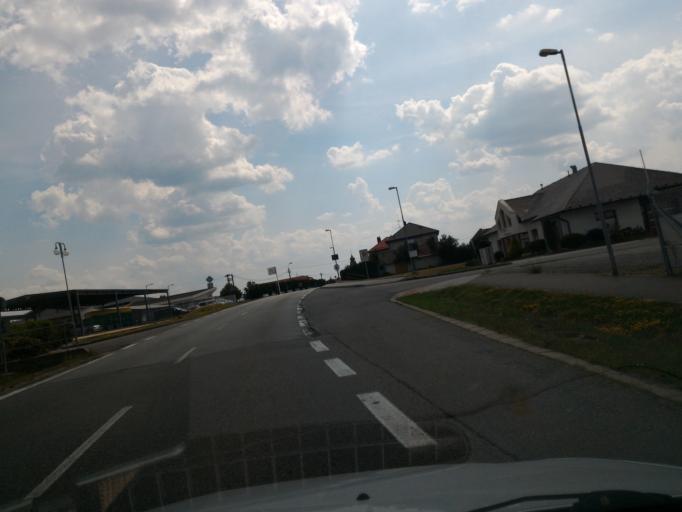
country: CZ
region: Vysocina
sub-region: Okres Zd'ar nad Sazavou
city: Nove Veseli
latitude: 49.5241
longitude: 15.9099
